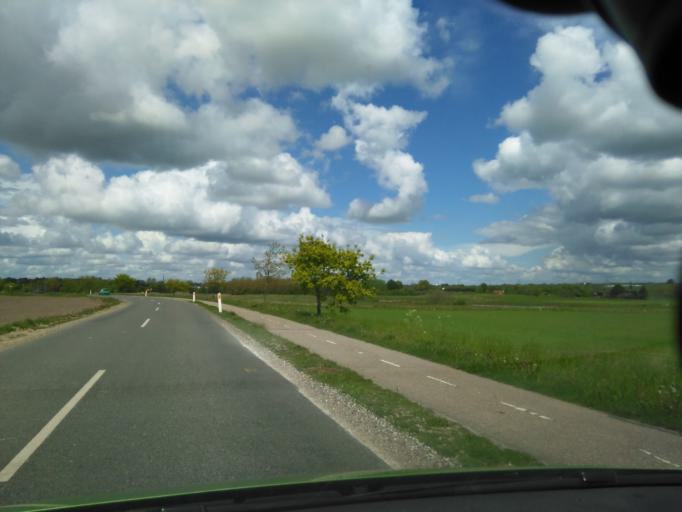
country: DK
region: Central Jutland
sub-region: Skanderborg Kommune
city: Horning
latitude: 56.0769
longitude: 10.0521
